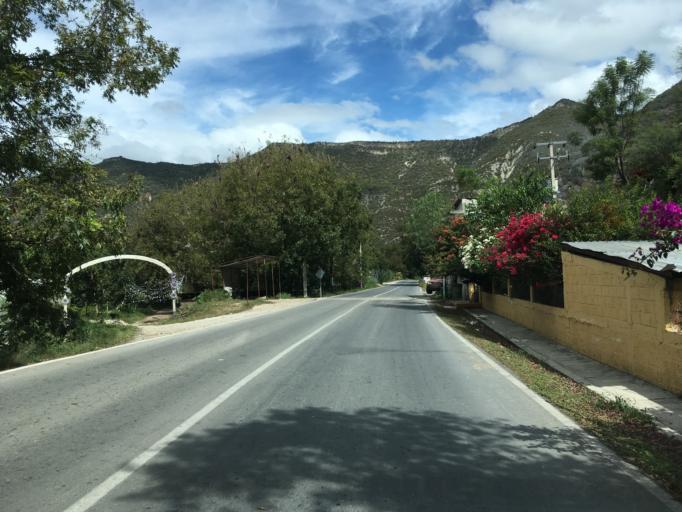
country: MX
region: Hidalgo
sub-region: San Agustin Metzquititlan
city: Mezquititlan
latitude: 20.5001
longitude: -98.7027
